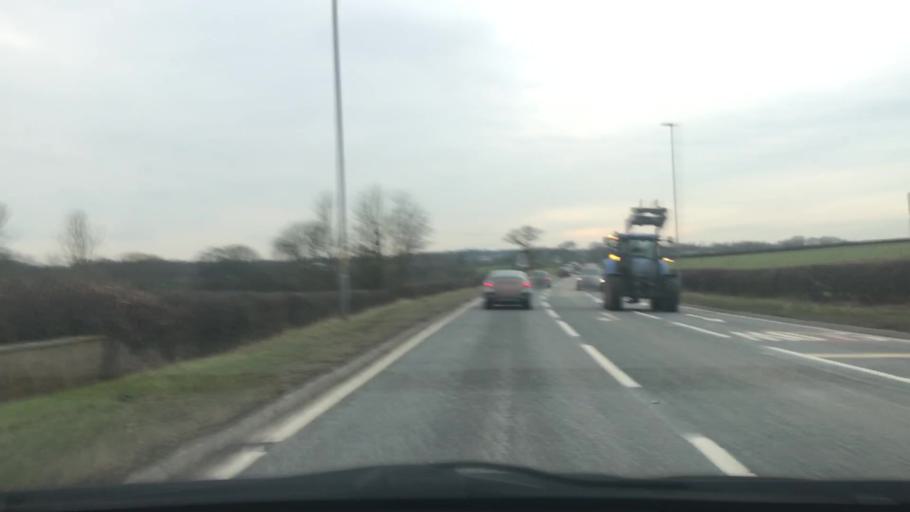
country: GB
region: England
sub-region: North Yorkshire
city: Knaresborough
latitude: 53.9809
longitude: -1.4763
